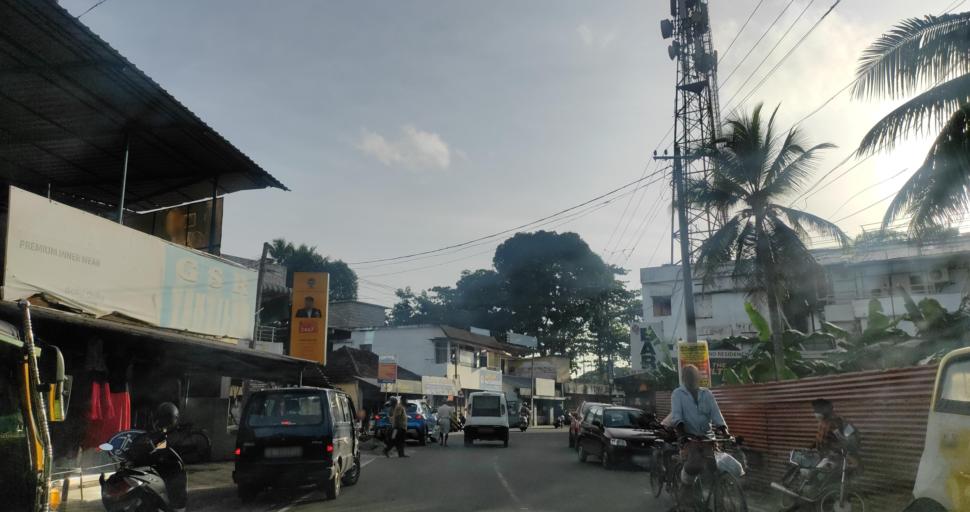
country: IN
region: Kerala
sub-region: Alappuzha
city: Shertallai
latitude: 9.6094
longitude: 76.3305
